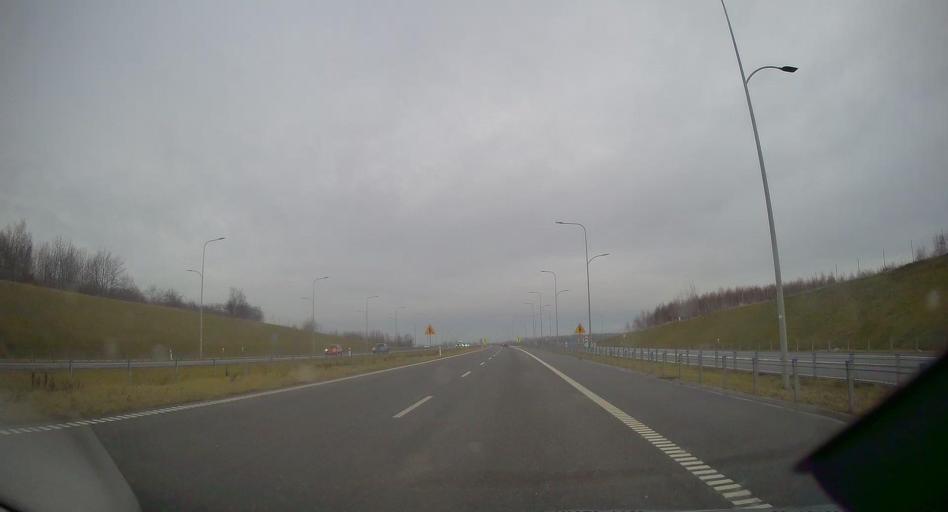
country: PL
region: Silesian Voivodeship
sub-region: Powiat czestochowski
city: Koscielec
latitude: 50.8810
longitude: 19.1575
